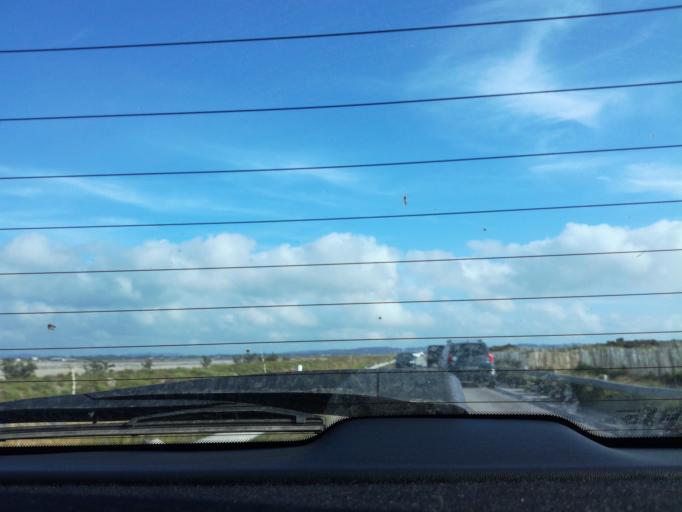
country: FR
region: Provence-Alpes-Cote d'Azur
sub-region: Departement du Var
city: Hyeres
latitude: 43.0768
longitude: 6.1269
